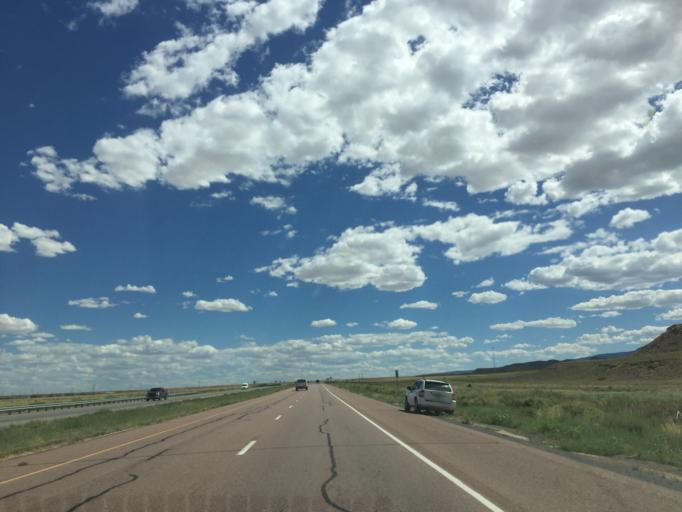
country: US
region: New Mexico
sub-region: McKinley County
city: Navajo
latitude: 36.1568
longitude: -108.7101
